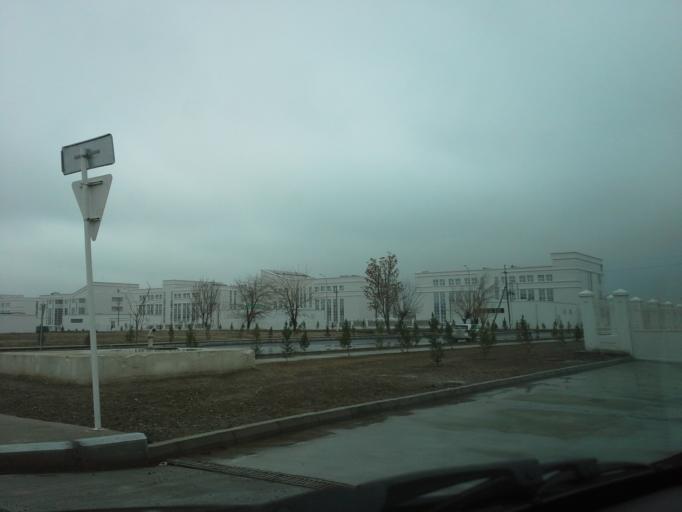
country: TM
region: Ahal
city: Ashgabat
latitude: 37.9551
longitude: 58.4273
